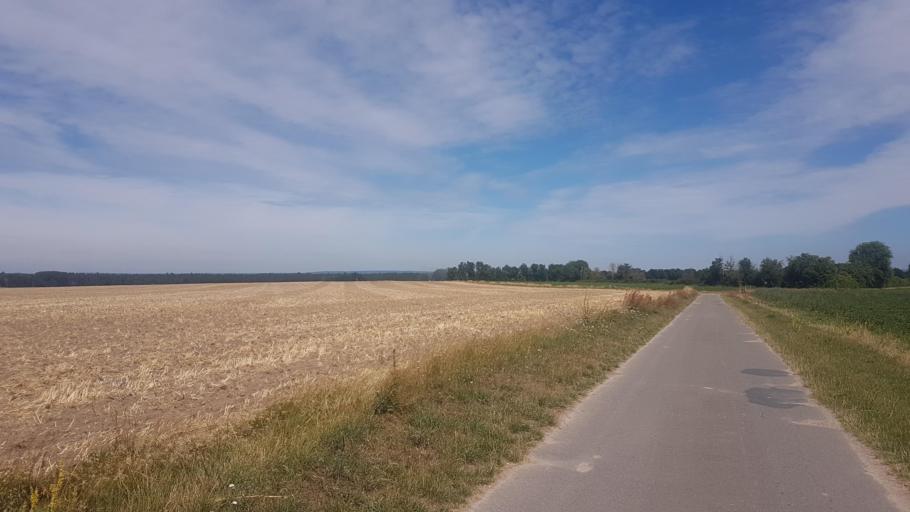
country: DE
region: Lower Saxony
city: Bleckede
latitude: 53.2597
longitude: 10.7623
